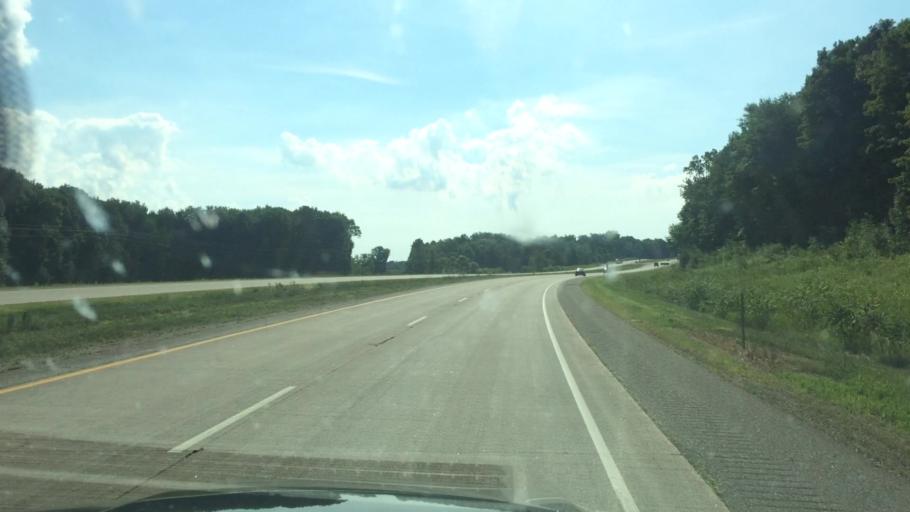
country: US
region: Wisconsin
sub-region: Shawano County
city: Wittenberg
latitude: 44.8258
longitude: -89.0695
